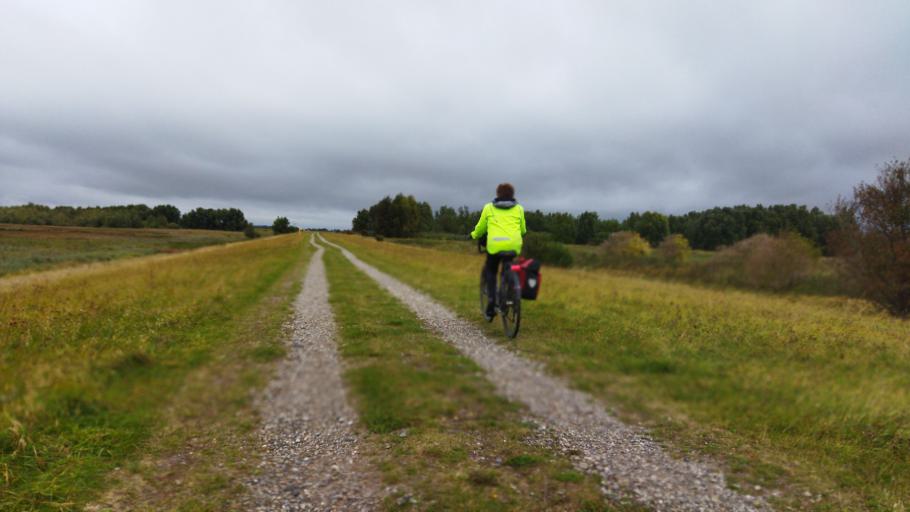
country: NL
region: Groningen
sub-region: Gemeente Delfzijl
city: Delfzijl
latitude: 53.3737
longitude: 7.0107
